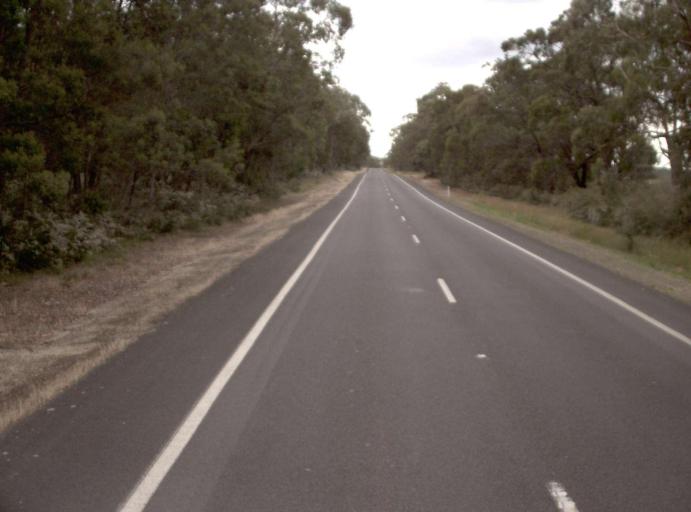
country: AU
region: Victoria
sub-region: Wellington
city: Sale
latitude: -38.3113
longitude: 147.0286
